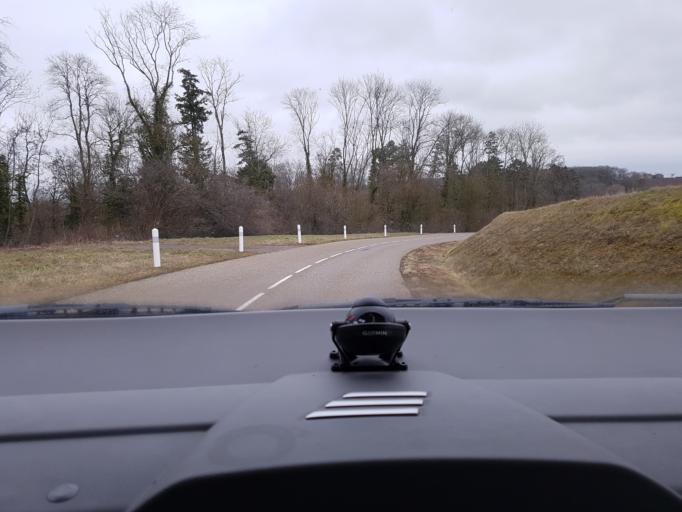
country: FR
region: Lorraine
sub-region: Departement de la Moselle
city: Morhange
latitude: 48.8703
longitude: 6.6632
